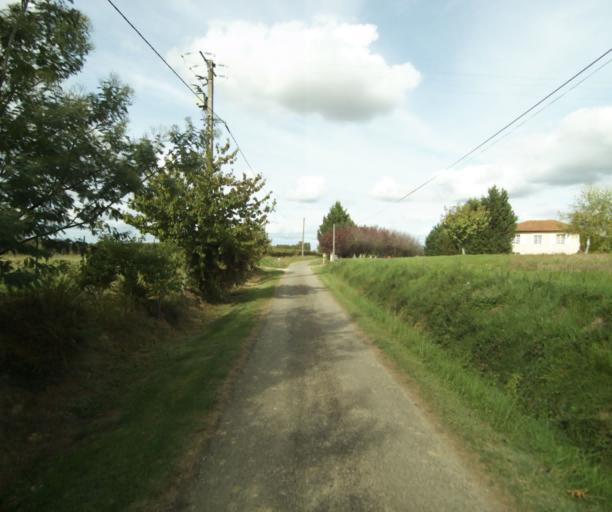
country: FR
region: Midi-Pyrenees
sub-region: Departement du Gers
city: Eauze
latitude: 43.8552
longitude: 0.1527
